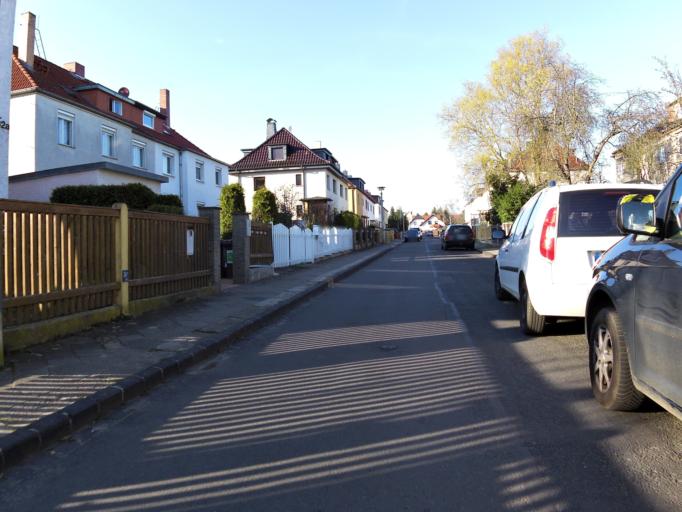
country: DE
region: Saxony
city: Markkleeberg
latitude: 51.2980
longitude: 12.3233
